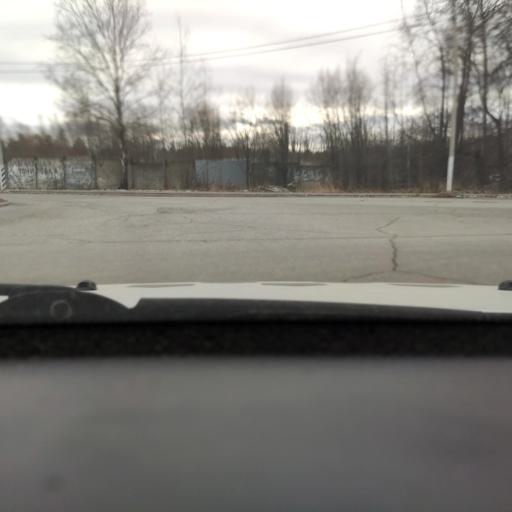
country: RU
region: Perm
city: Perm
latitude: 58.0949
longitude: 56.4025
